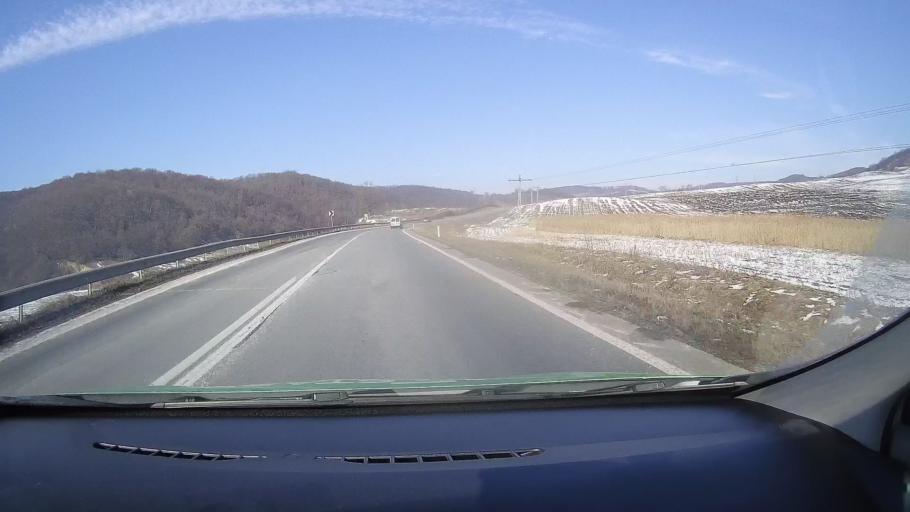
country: RO
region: Brasov
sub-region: Comuna Bunesti
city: Bunesti
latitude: 46.1338
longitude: 25.0164
